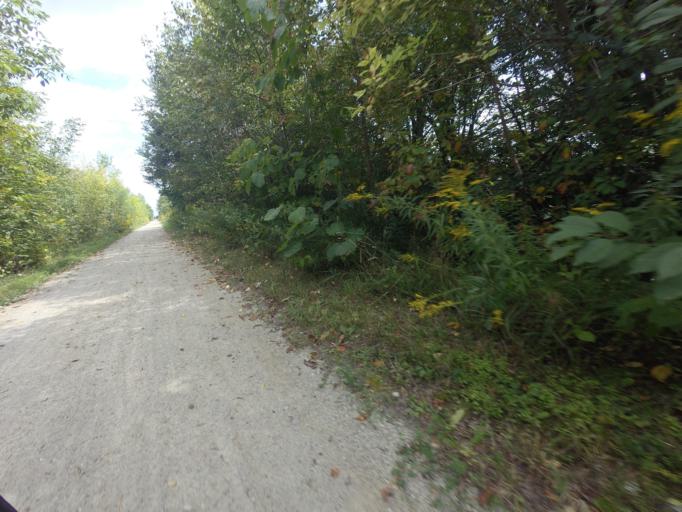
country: CA
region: Ontario
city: North Perth
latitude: 43.5758
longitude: -80.8150
